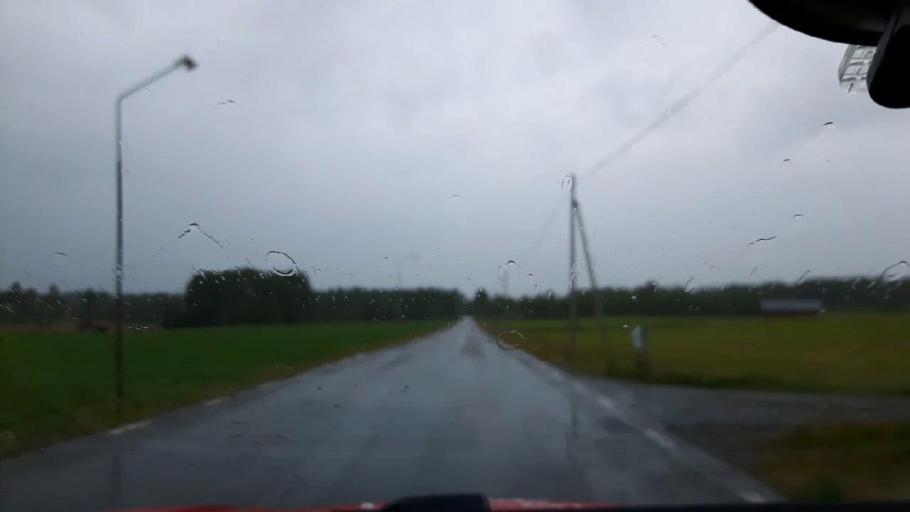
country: SE
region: Jaemtland
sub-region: OEstersunds Kommun
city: Brunflo
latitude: 62.9927
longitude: 14.7908
